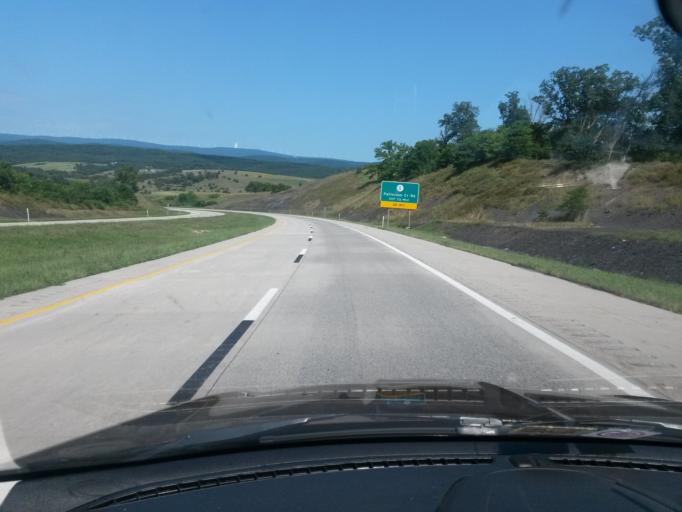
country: US
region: West Virginia
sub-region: Hardy County
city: Moorefield
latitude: 39.1411
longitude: -79.0633
